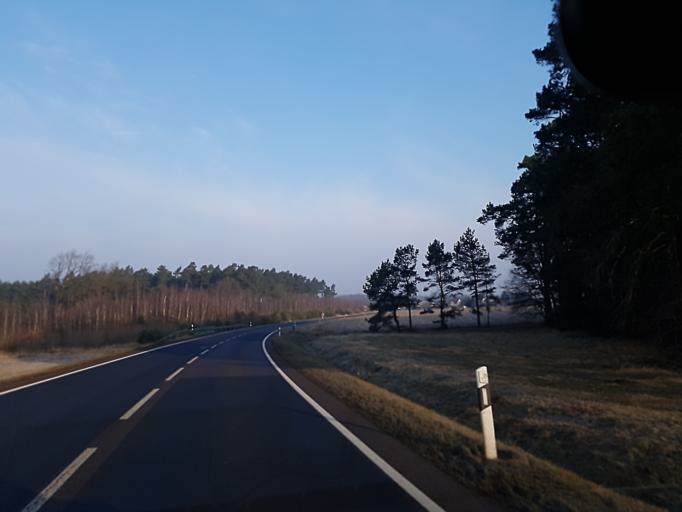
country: DE
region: Brandenburg
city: Wiesenburg
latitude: 52.0833
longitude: 12.4460
